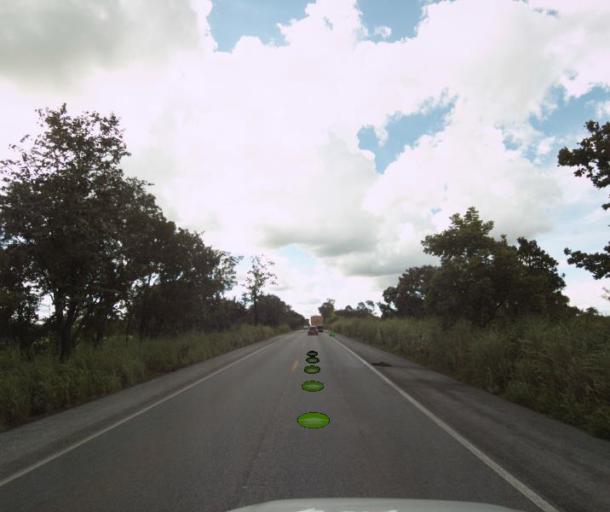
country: BR
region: Goias
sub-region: Porangatu
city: Porangatu
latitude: -13.1981
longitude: -49.1589
